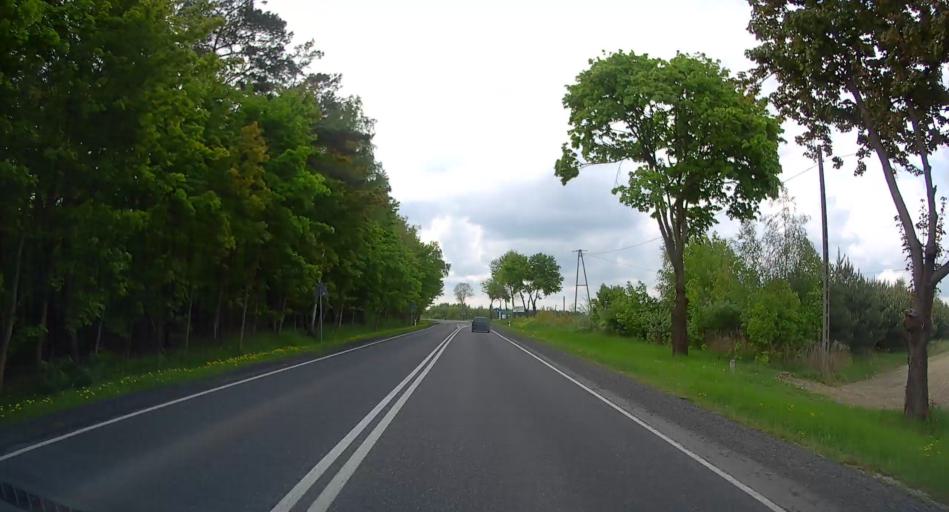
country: PL
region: Masovian Voivodeship
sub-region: Powiat nowodworski
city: Zakroczym
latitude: 52.4459
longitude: 20.5808
